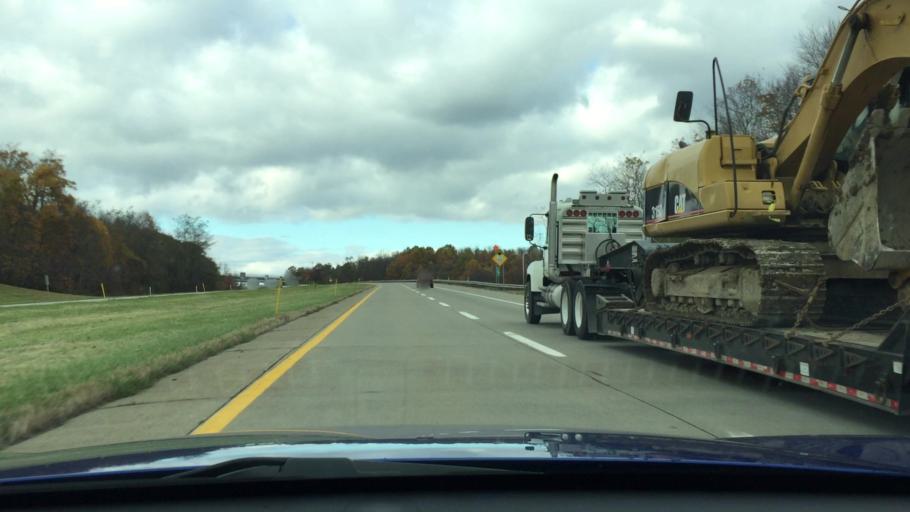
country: US
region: Pennsylvania
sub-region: Westmoreland County
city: New Stanton
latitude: 40.2601
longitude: -79.6132
